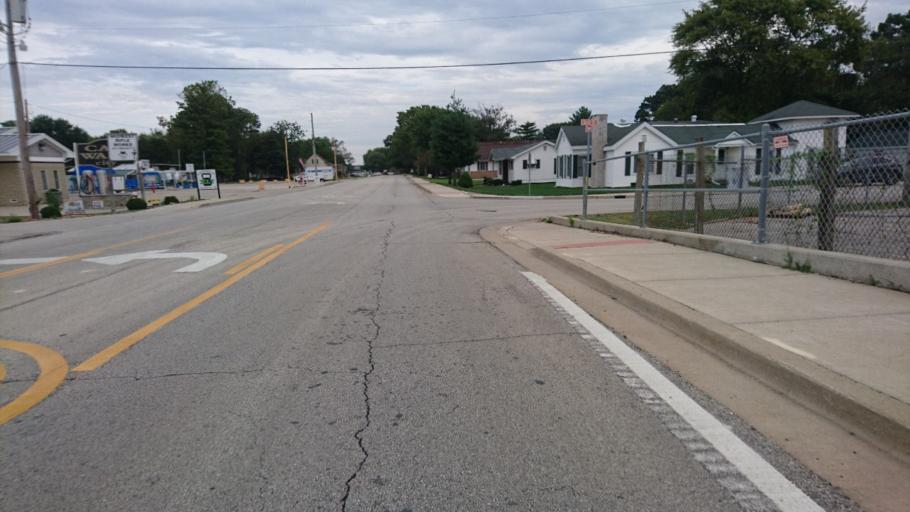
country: US
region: Illinois
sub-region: Sangamon County
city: Chatham
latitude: 39.6763
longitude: -89.7022
